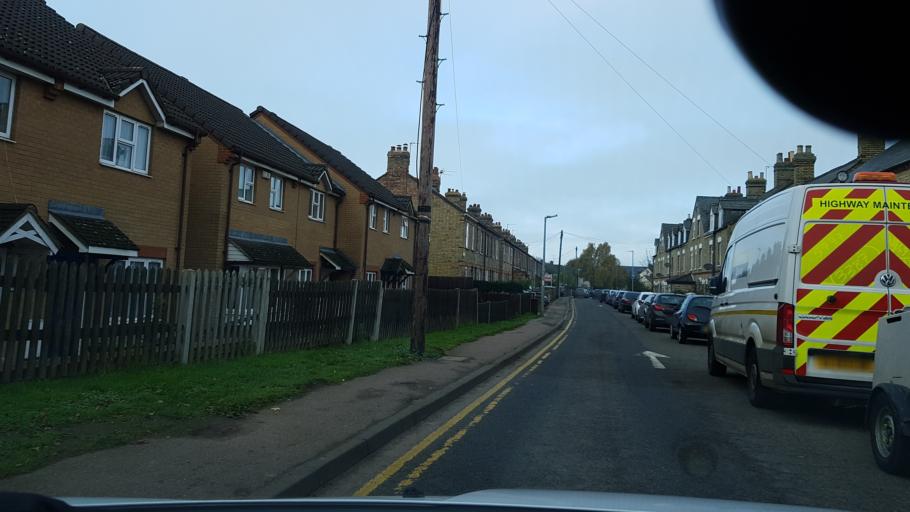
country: GB
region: England
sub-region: Central Bedfordshire
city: Biggleswade
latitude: 52.0896
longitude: -0.2631
